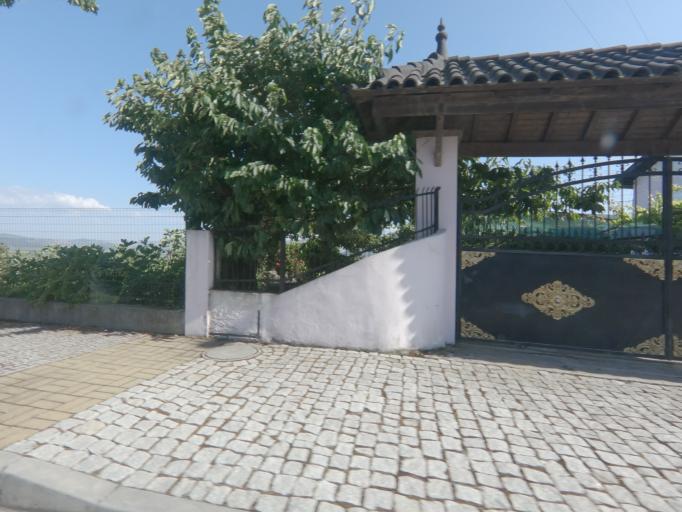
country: PT
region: Vila Real
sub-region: Sabrosa
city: Sabrosa
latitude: 41.2623
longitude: -7.5805
